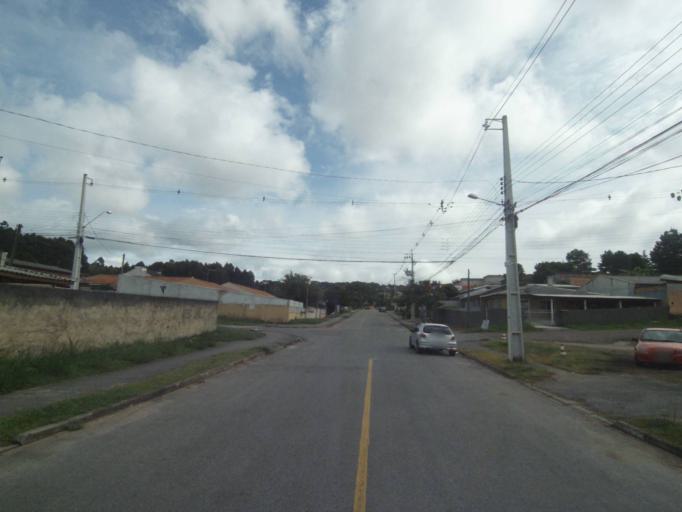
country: BR
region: Parana
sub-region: Quatro Barras
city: Quatro Barras
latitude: -25.3449
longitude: -49.0759
